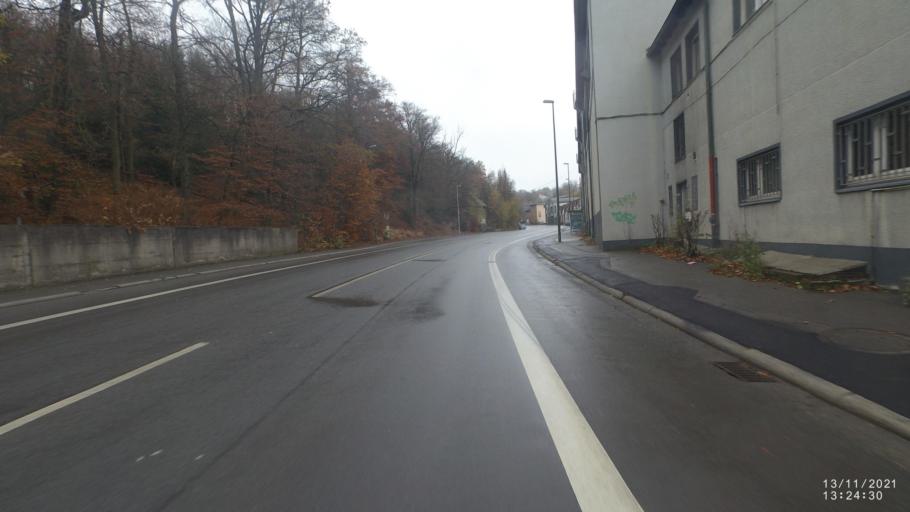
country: DE
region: North Rhine-Westphalia
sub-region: Regierungsbezirk Arnsberg
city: Luedenscheid
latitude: 51.2337
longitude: 7.6331
